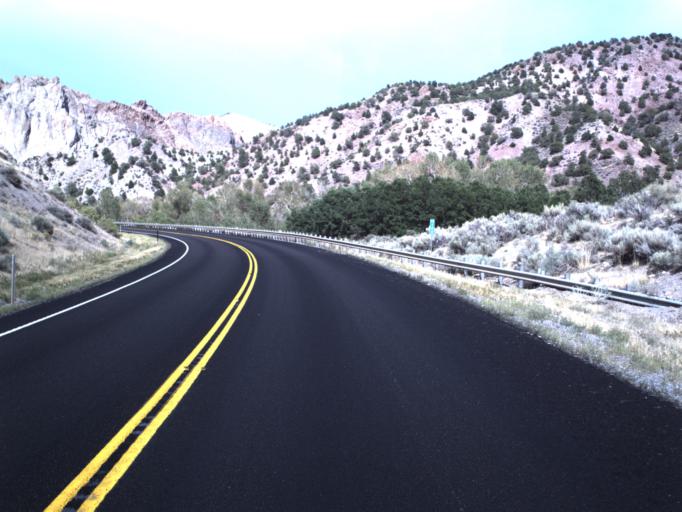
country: US
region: Utah
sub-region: Sevier County
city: Monroe
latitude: 38.5639
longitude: -112.2704
